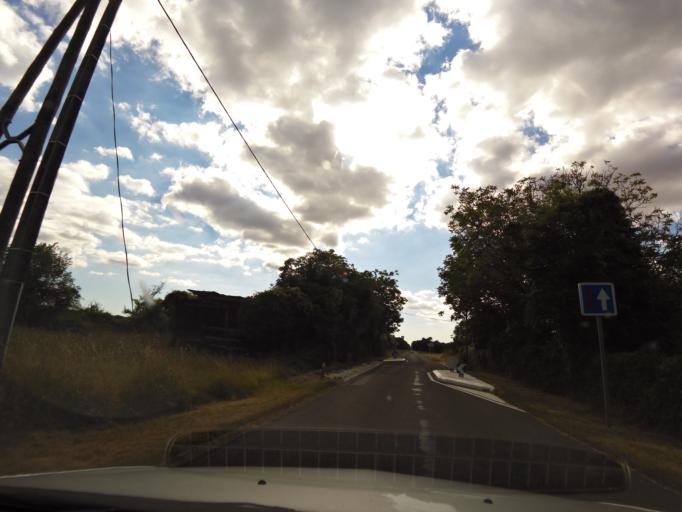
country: FR
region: Poitou-Charentes
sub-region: Departement des Deux-Sevres
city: Beauvoir-sur-Niort
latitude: 46.1485
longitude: -0.4087
